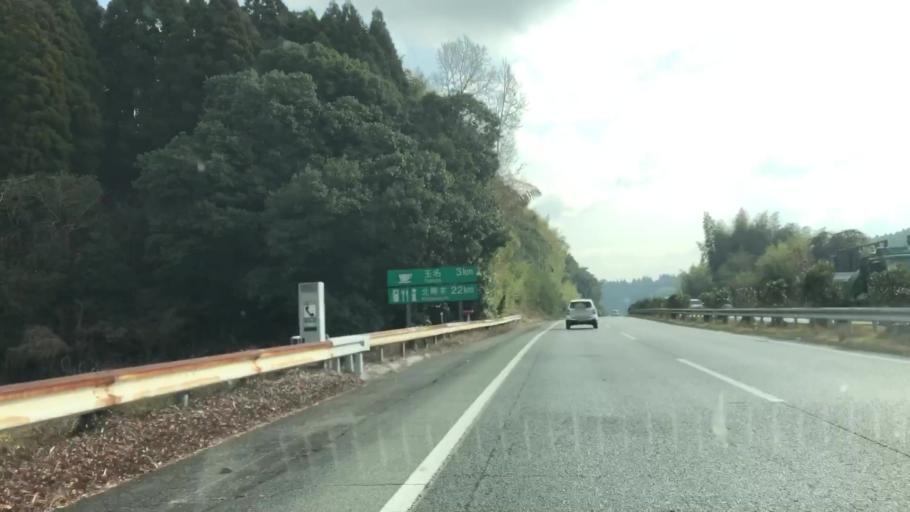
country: JP
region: Kumamoto
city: Yamaga
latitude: 33.0376
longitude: 130.5710
